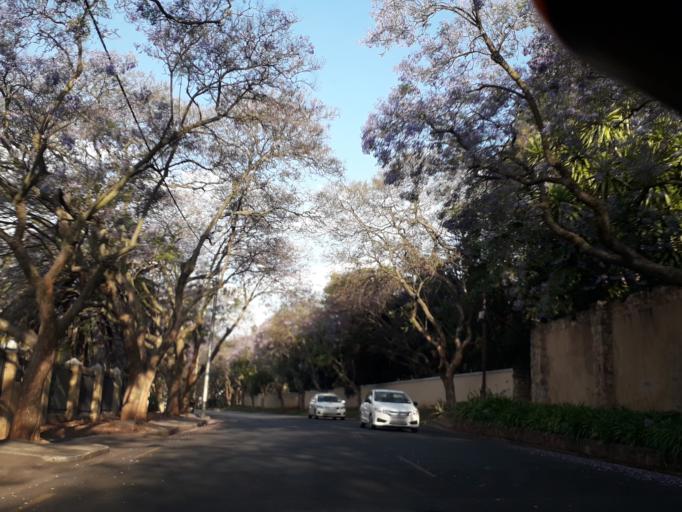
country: ZA
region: Gauteng
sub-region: City of Johannesburg Metropolitan Municipality
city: Johannesburg
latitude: -26.1706
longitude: 28.0595
